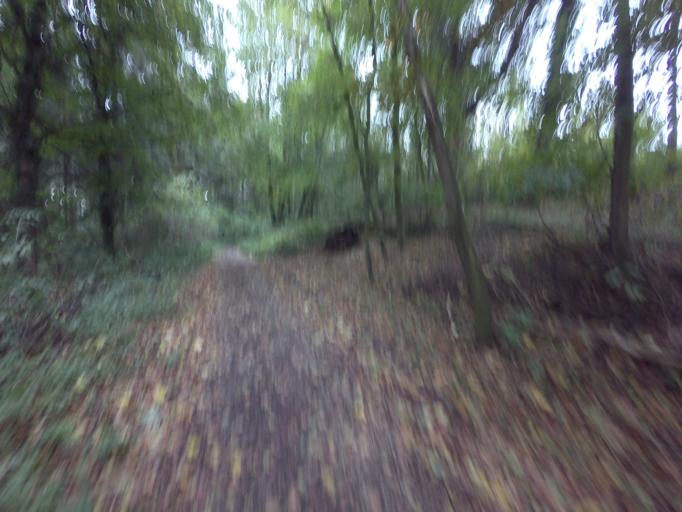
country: DE
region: North Rhine-Westphalia
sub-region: Regierungsbezirk Koln
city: Ubach-Palenberg
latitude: 50.9125
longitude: 6.0954
